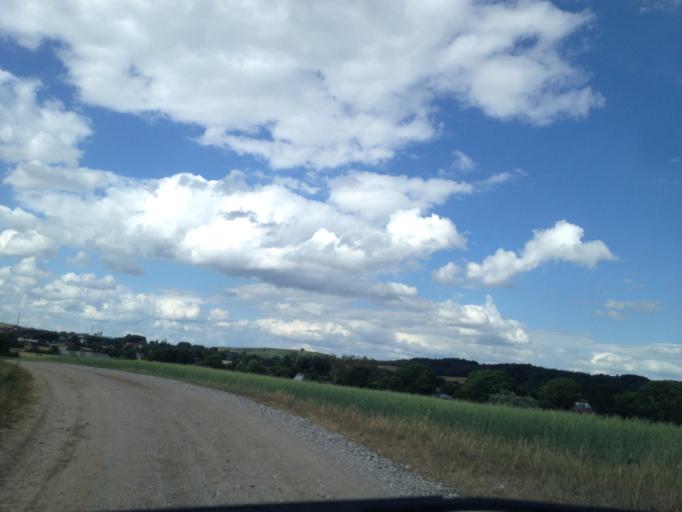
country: DK
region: Central Jutland
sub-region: Syddjurs Kommune
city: Ronde
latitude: 56.2021
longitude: 10.4845
